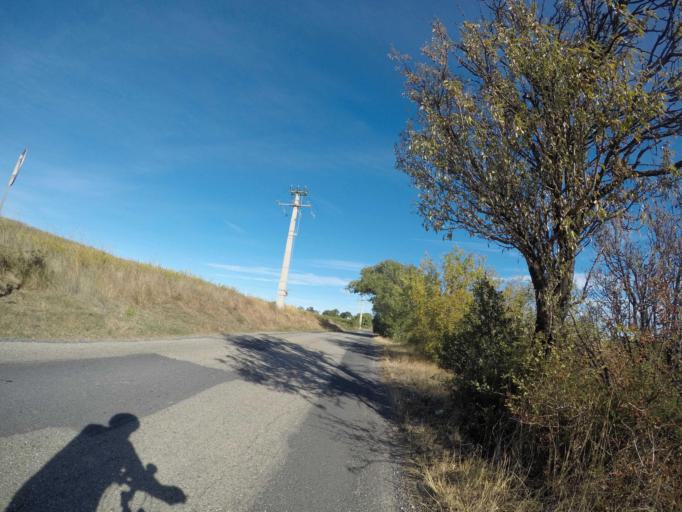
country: FR
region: Languedoc-Roussillon
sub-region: Departement des Pyrenees-Orientales
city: Trouillas
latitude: 42.5986
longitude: 2.8074
